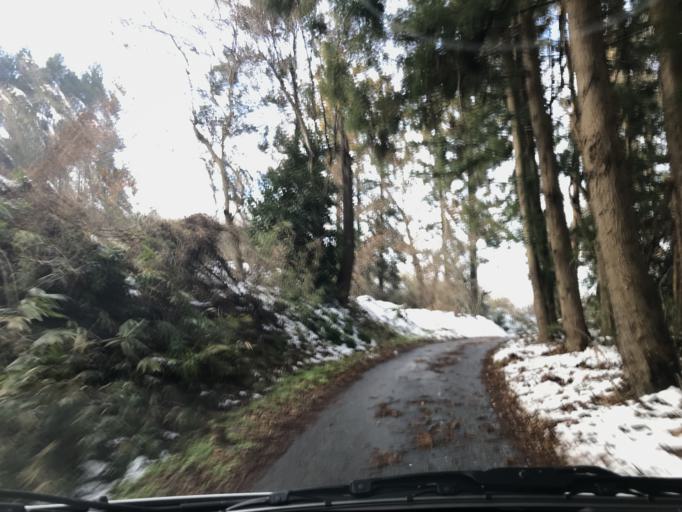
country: JP
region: Iwate
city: Mizusawa
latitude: 39.0318
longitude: 141.1071
